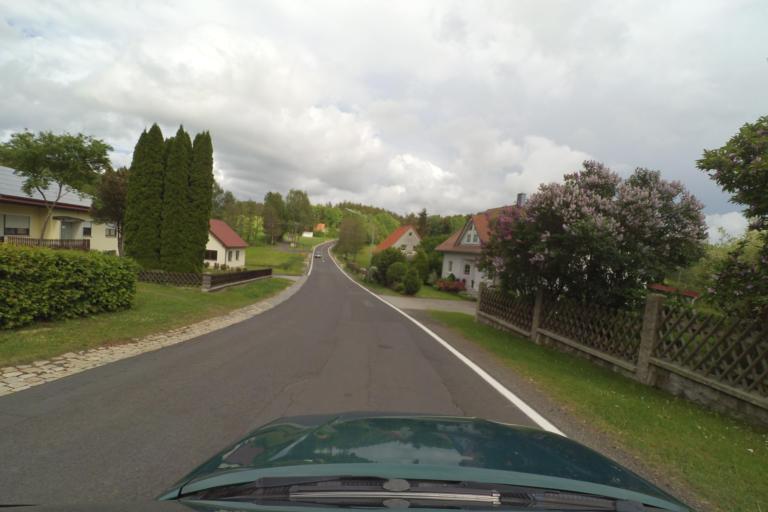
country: DE
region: Bavaria
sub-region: Upper Palatinate
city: Schwarzenbach
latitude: 49.8378
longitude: 12.3814
